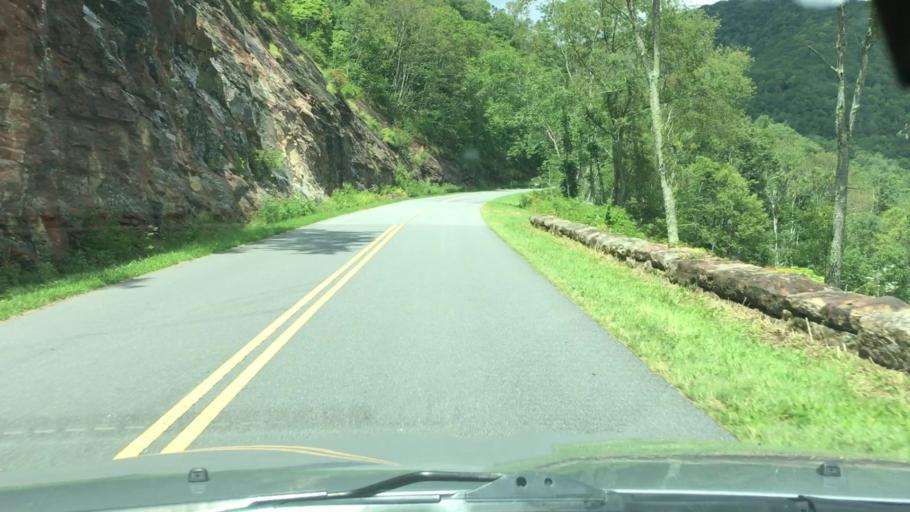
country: US
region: North Carolina
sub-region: Buncombe County
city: Swannanoa
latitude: 35.6902
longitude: -82.4093
